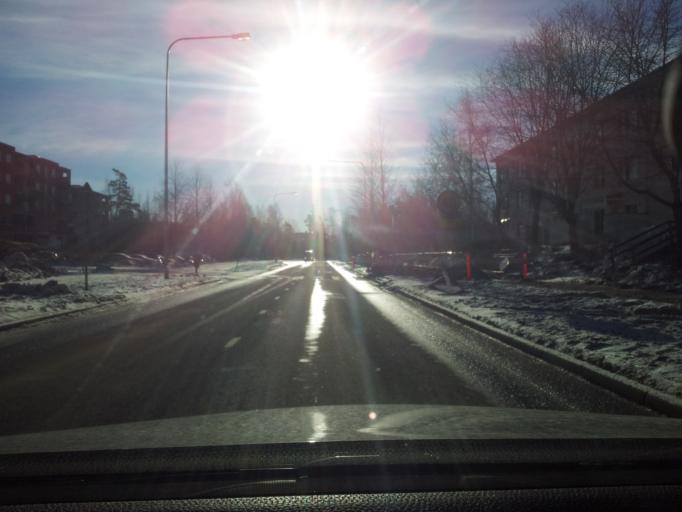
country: FI
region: Uusimaa
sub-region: Helsinki
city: Koukkuniemi
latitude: 60.1551
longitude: 24.7279
